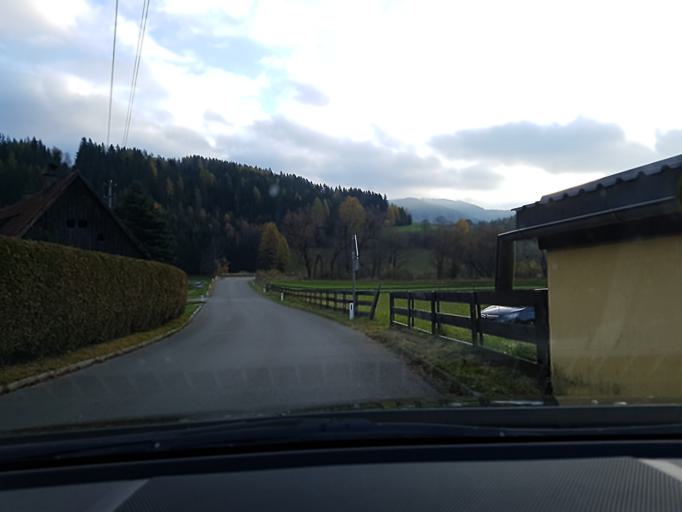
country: AT
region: Styria
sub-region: Politischer Bezirk Murtal
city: Oberzeiring
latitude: 47.2780
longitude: 14.4820
